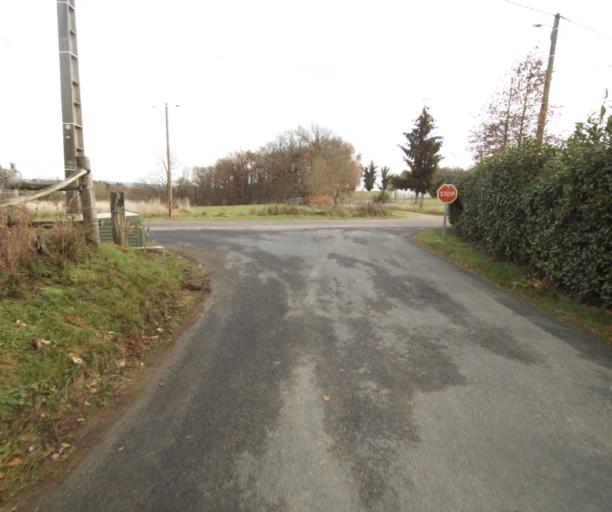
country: FR
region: Limousin
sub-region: Departement de la Correze
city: Chameyrat
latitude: 45.2406
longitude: 1.6994
